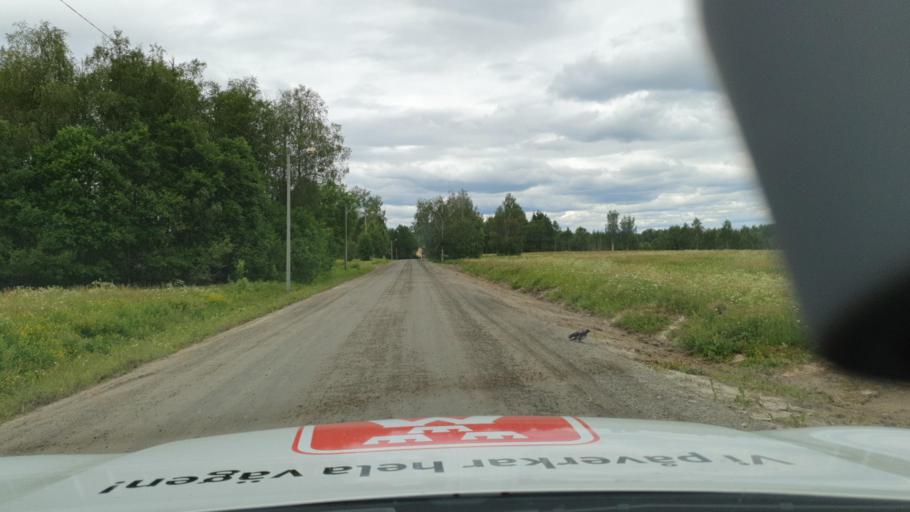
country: SE
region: Vaesterbotten
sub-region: Nordmalings Kommun
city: Nordmaling
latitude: 63.7108
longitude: 19.4315
